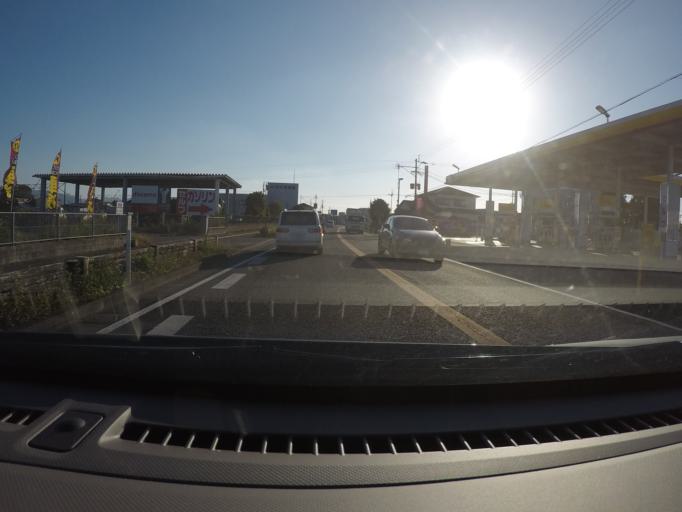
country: JP
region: Kagoshima
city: Izumi
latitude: 32.1226
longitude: 130.3415
